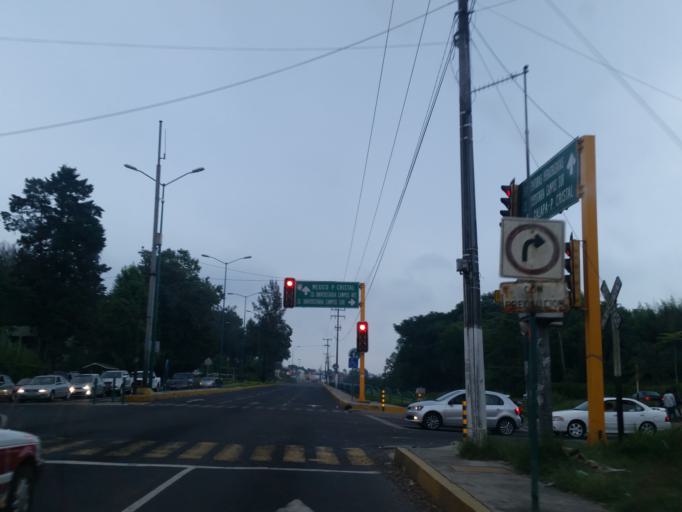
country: MX
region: Veracruz
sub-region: Xalapa
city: Xalapa de Enriquez
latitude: 19.5146
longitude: -96.9181
